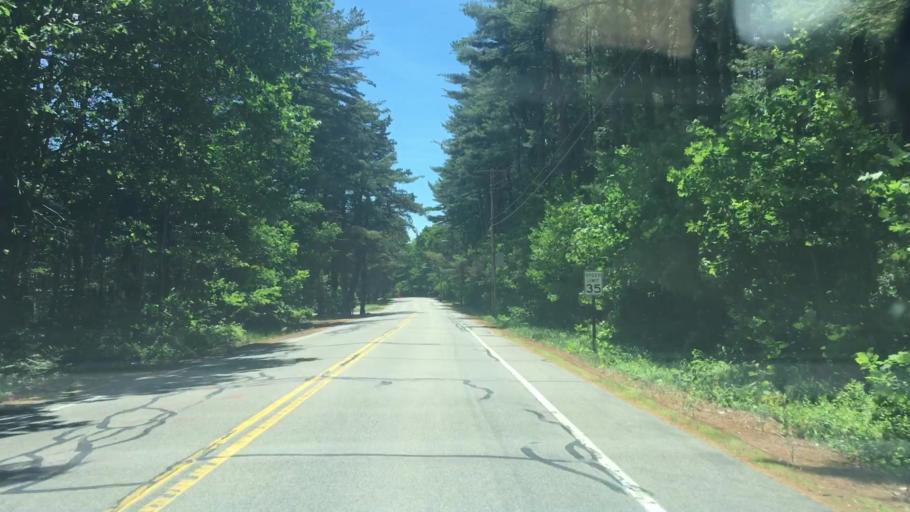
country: US
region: Maine
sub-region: York County
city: Kennebunk
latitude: 43.3712
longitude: -70.5267
